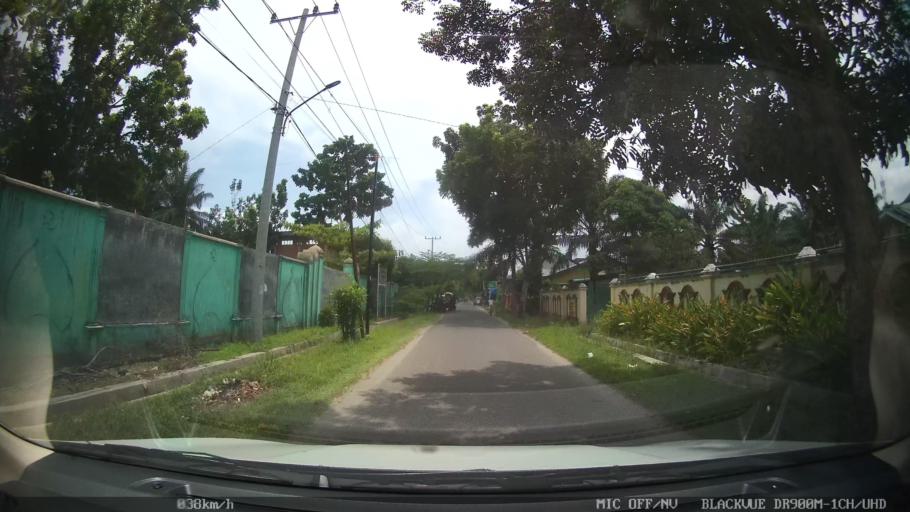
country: ID
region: North Sumatra
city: Binjai
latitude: 3.6208
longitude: 98.5080
